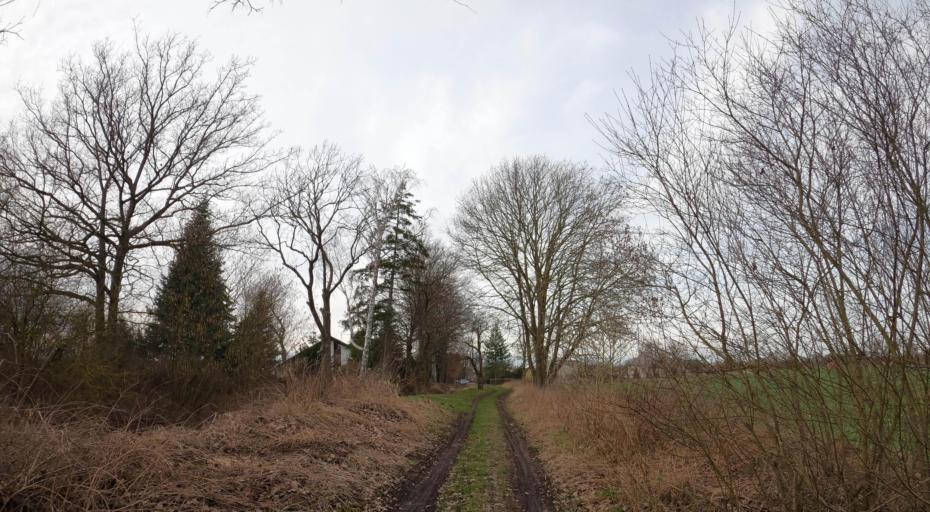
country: PL
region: West Pomeranian Voivodeship
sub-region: Powiat pyrzycki
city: Pyrzyce
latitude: 53.1335
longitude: 14.9007
